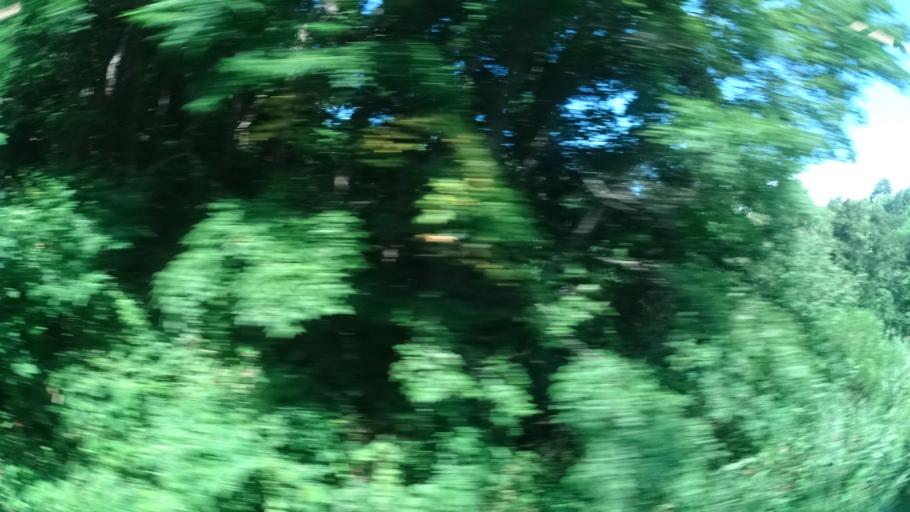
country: JP
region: Fukushima
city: Iwaki
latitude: 37.2454
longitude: 141.0075
